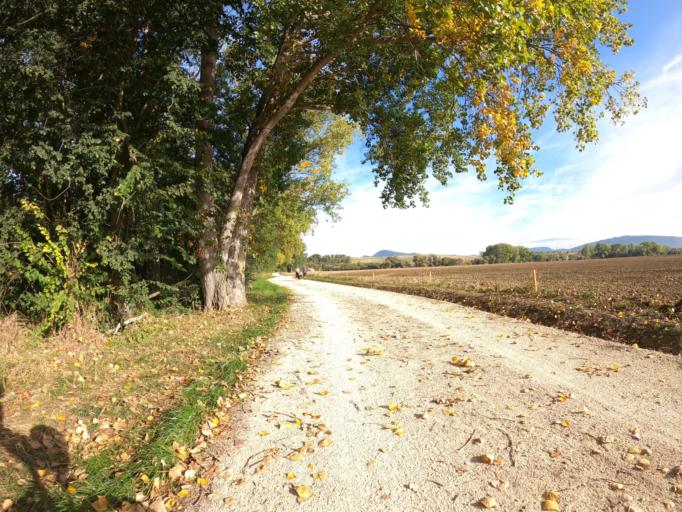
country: ES
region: Navarre
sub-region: Provincia de Navarra
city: Orkoien
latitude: 42.8135
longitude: -1.7389
